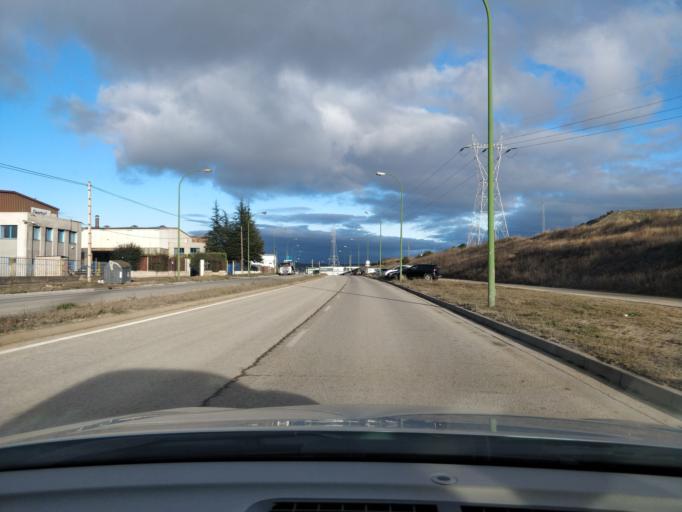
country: ES
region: Castille and Leon
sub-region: Provincia de Burgos
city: Sotragero
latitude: 42.3662
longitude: -3.7333
